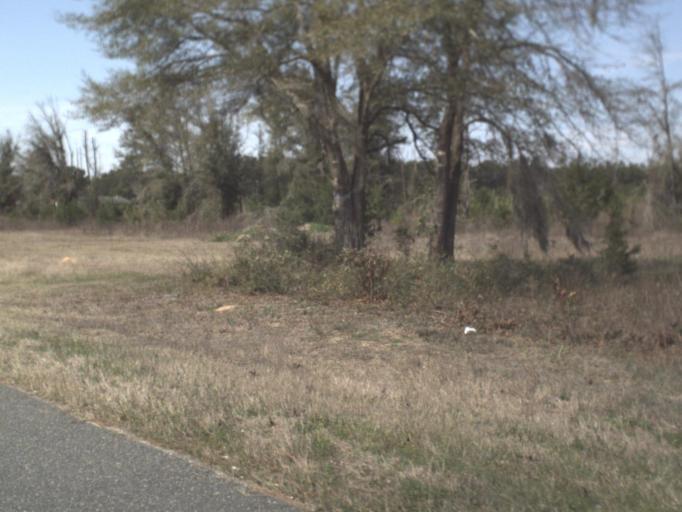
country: US
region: Florida
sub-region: Gadsden County
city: Gretna
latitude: 30.5271
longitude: -84.7927
